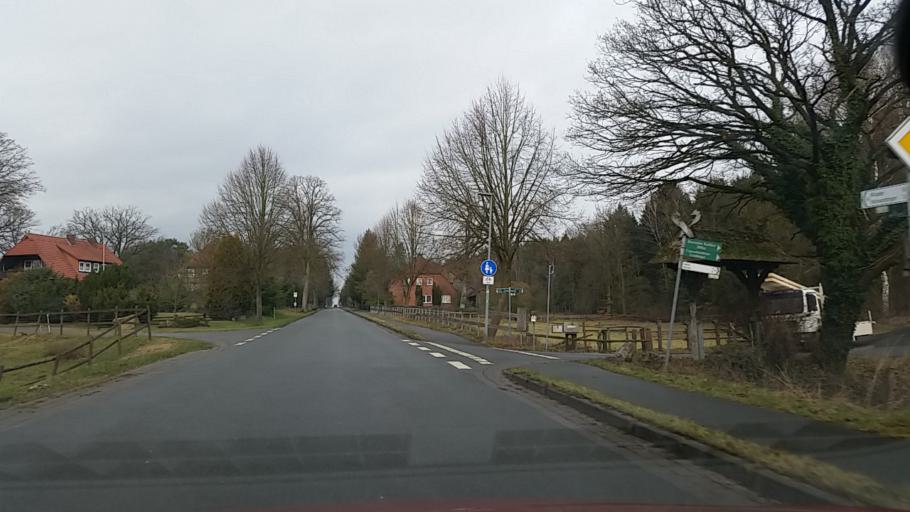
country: DE
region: Lower Saxony
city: Bispingen
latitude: 53.1039
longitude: 10.0035
